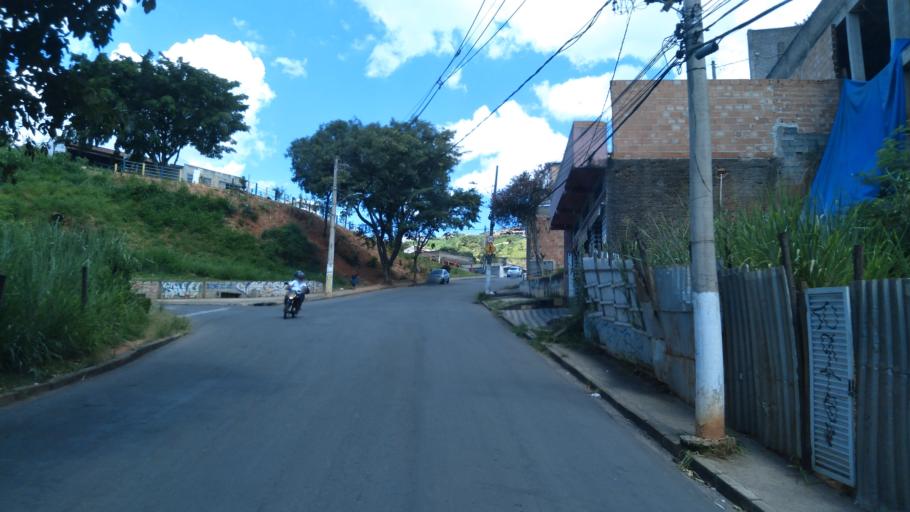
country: BR
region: Minas Gerais
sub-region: Belo Horizonte
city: Belo Horizonte
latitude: -19.8441
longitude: -43.8973
